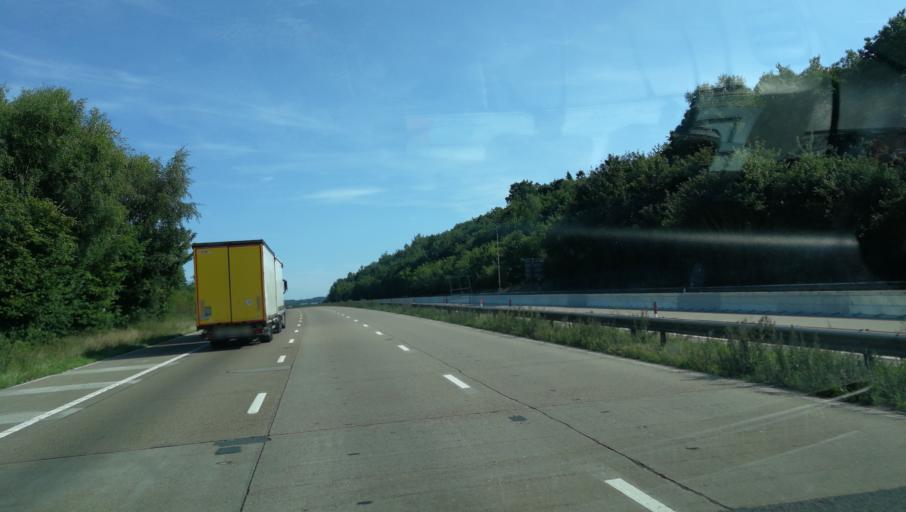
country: GB
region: England
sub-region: Kent
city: Harrietsham
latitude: 51.2522
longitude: 0.6374
